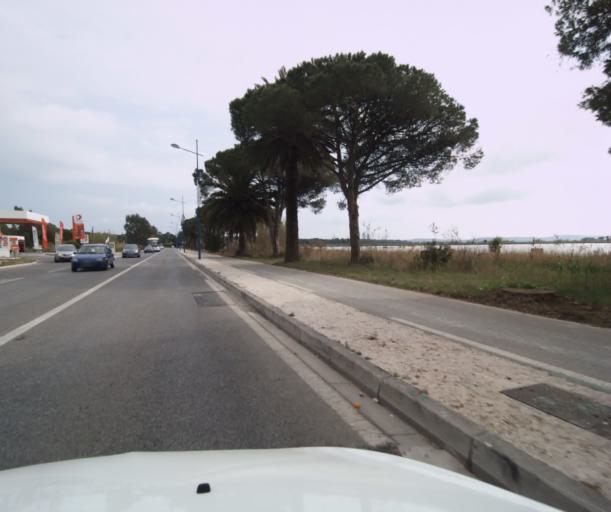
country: FR
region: Provence-Alpes-Cote d'Azur
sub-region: Departement du Var
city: Hyeres
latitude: 43.0853
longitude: 6.1478
